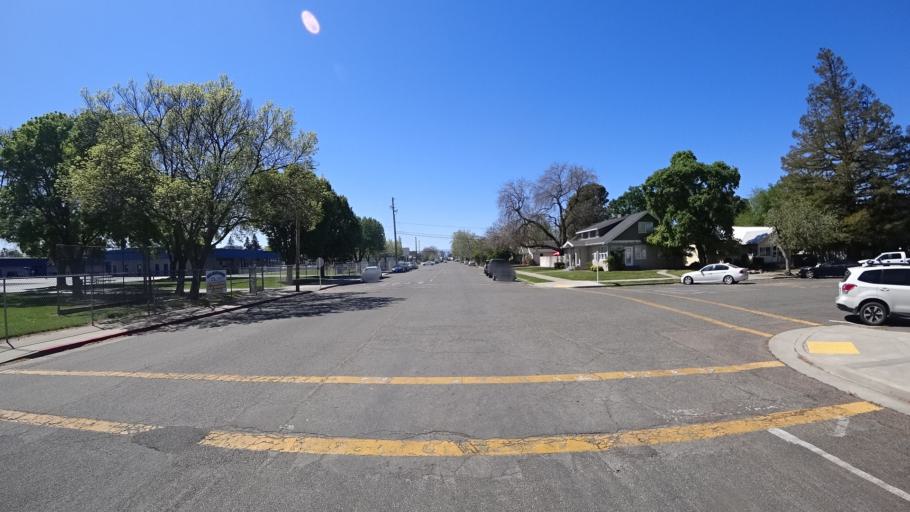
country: US
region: California
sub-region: Glenn County
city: Orland
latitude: 39.7463
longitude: -122.1900
